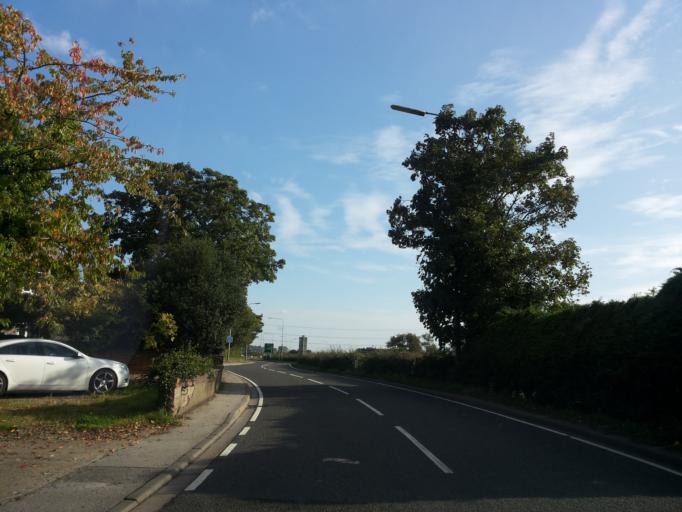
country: GB
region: England
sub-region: North Yorkshire
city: Camblesforth
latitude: 53.7243
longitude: -1.0218
